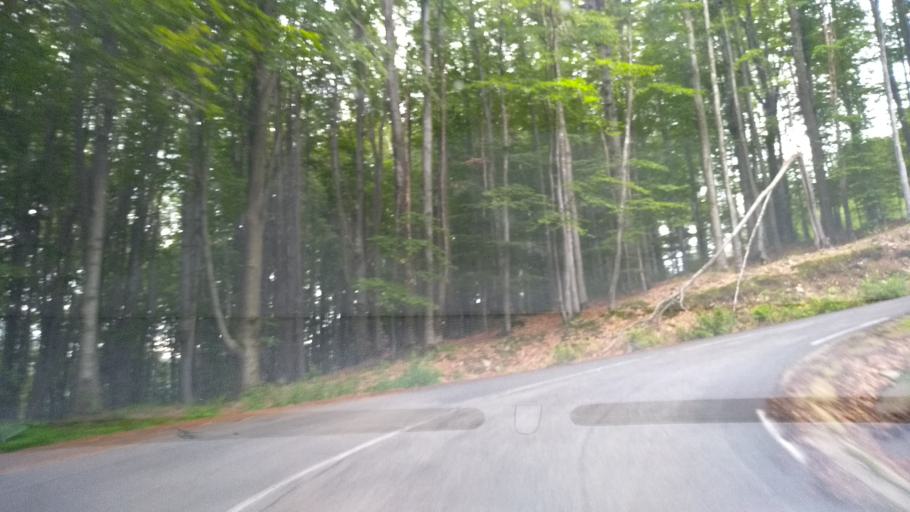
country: RO
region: Hunedoara
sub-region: Municipiul  Vulcan
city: Jiu-Paroseni
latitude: 45.3359
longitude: 23.2919
